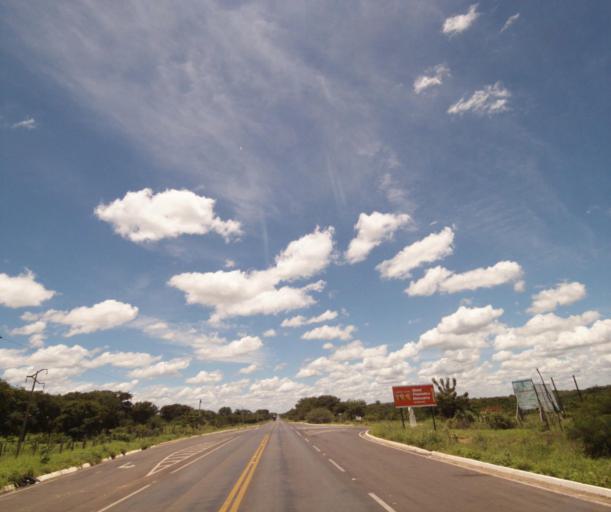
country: BR
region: Bahia
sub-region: Bom Jesus Da Lapa
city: Bom Jesus da Lapa
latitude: -13.2612
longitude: -43.5178
